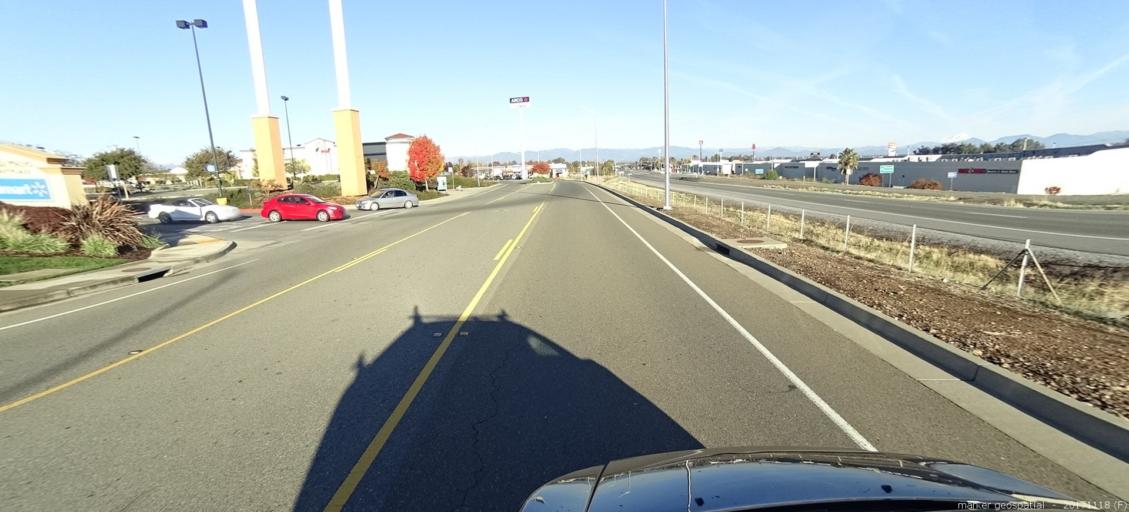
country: US
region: California
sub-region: Shasta County
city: Anderson
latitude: 40.4321
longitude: -122.2870
